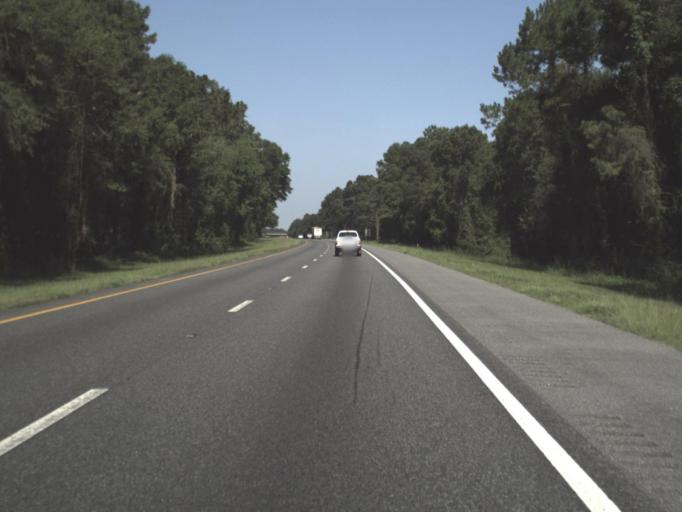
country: US
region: Florida
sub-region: Suwannee County
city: Wellborn
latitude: 30.2860
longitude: -82.8368
